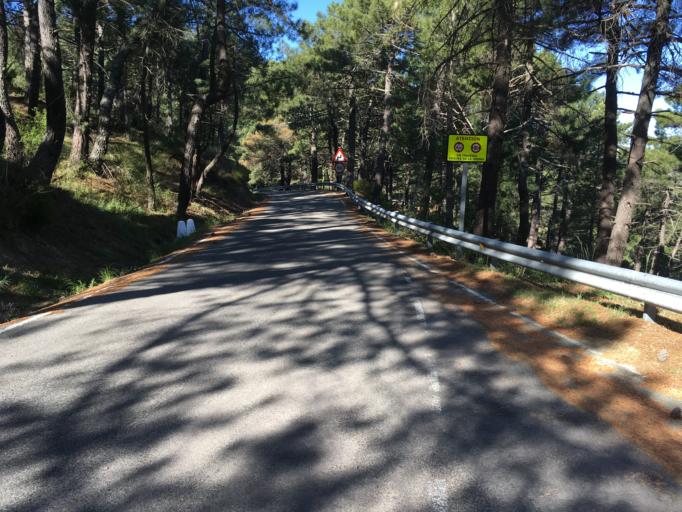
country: ES
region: Andalusia
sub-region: Provincia de Jaen
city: Segura de la Sierra
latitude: 38.3110
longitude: -2.6062
